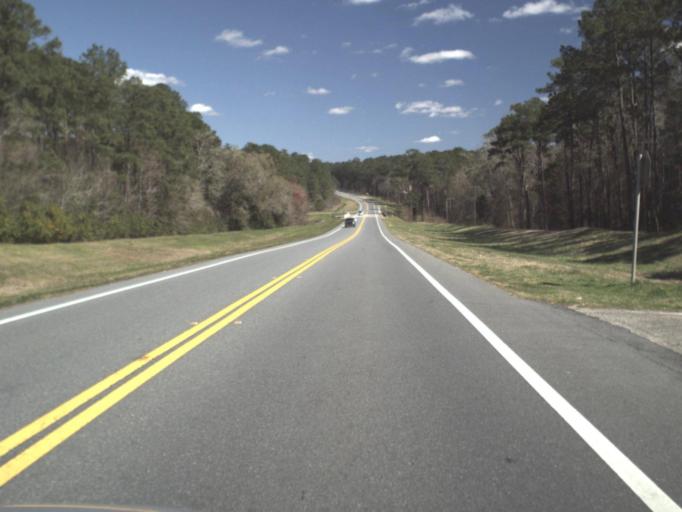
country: US
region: Florida
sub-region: Gadsden County
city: Chattahoochee
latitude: 30.7011
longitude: -84.8299
